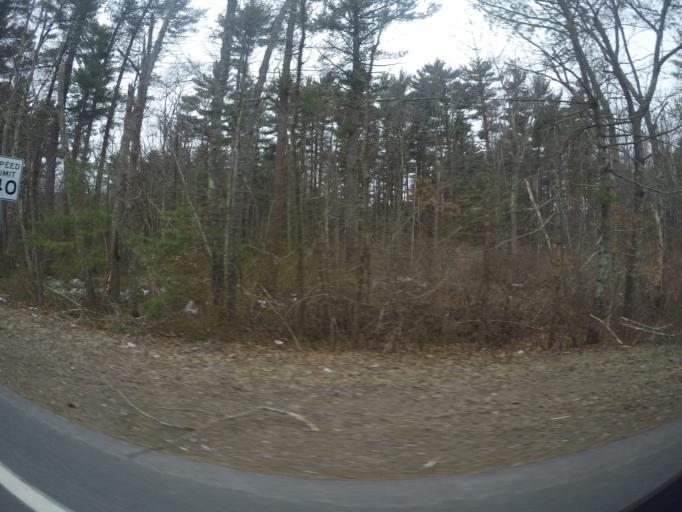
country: US
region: Massachusetts
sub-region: Bristol County
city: Easton
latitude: 42.0151
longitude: -71.0908
